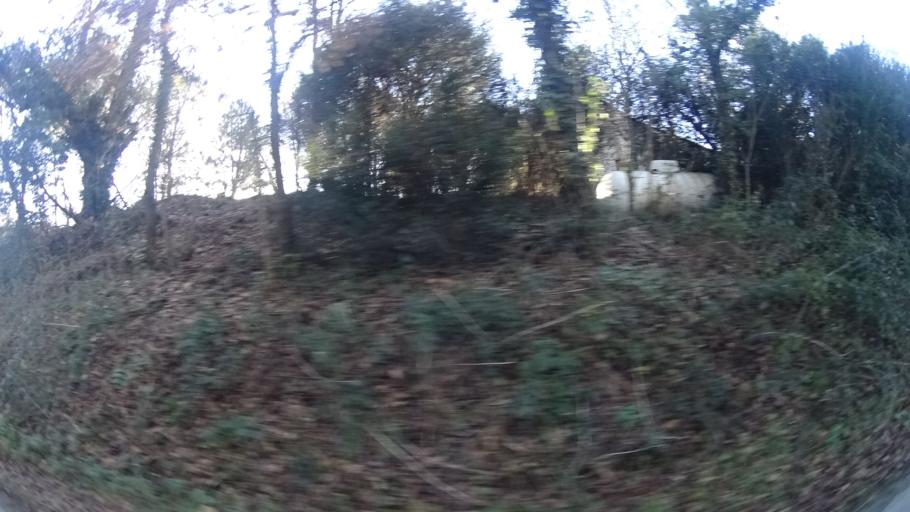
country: FR
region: Brittany
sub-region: Departement du Morbihan
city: Allaire
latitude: 47.6565
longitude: -2.1591
